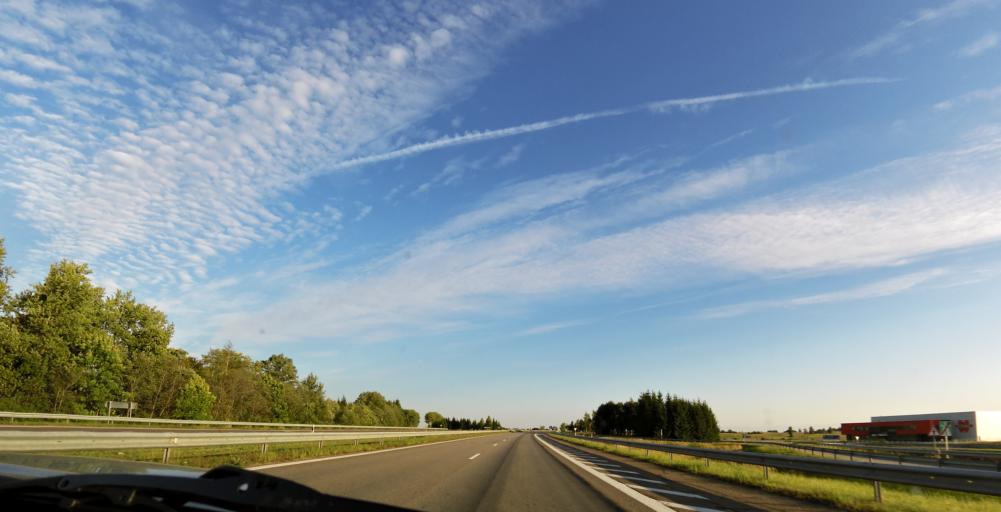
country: LT
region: Vilnius County
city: Ukmerge
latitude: 55.1766
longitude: 24.8122
